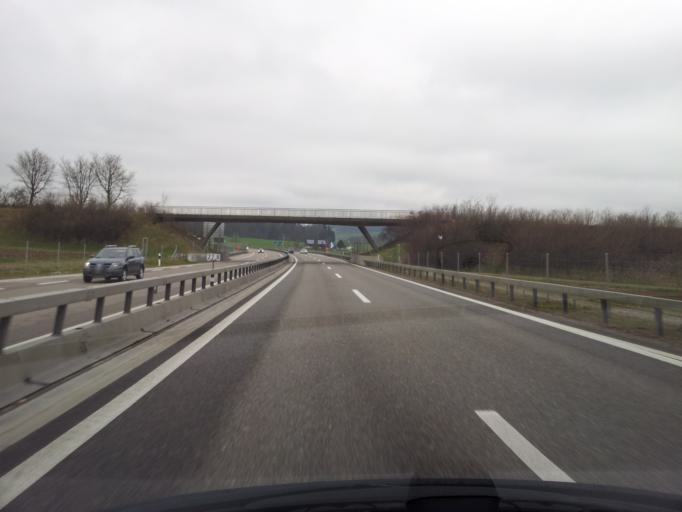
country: CH
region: Zurich
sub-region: Bezirk Andelfingen
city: Kleinandelfingen
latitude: 47.6206
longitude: 8.6828
